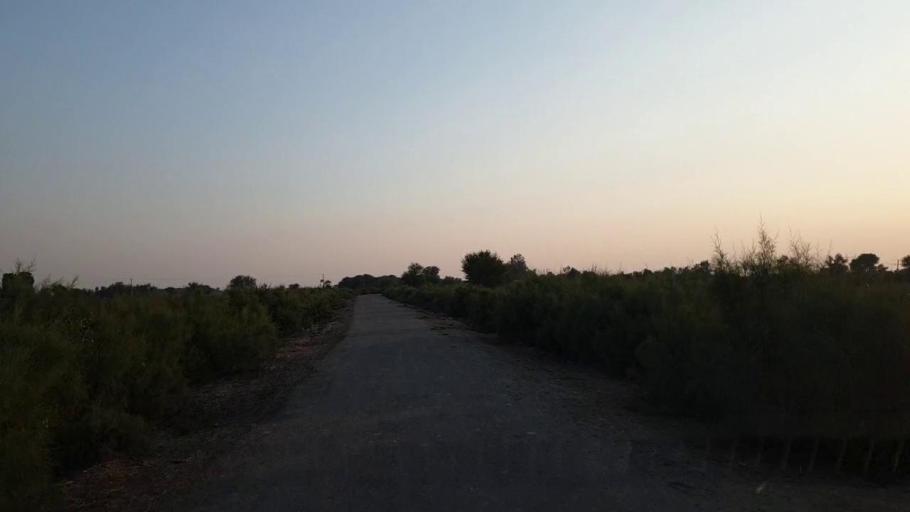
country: PK
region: Sindh
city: Sehwan
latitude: 26.4517
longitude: 67.7688
